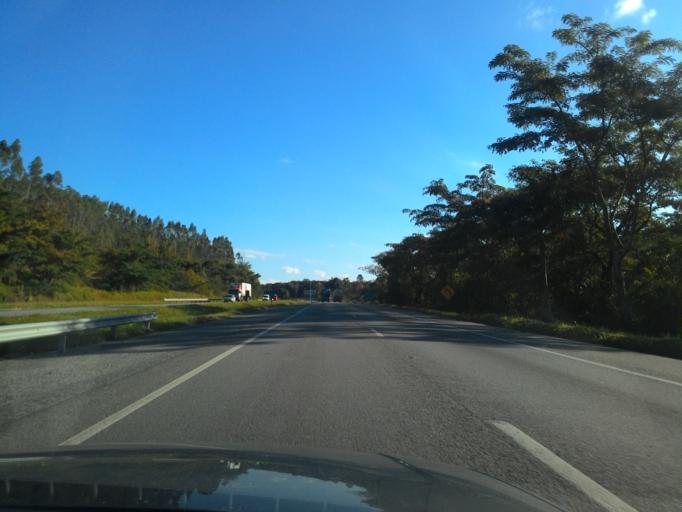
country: BR
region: Sao Paulo
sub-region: Registro
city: Registro
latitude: -24.5670
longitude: -47.8749
